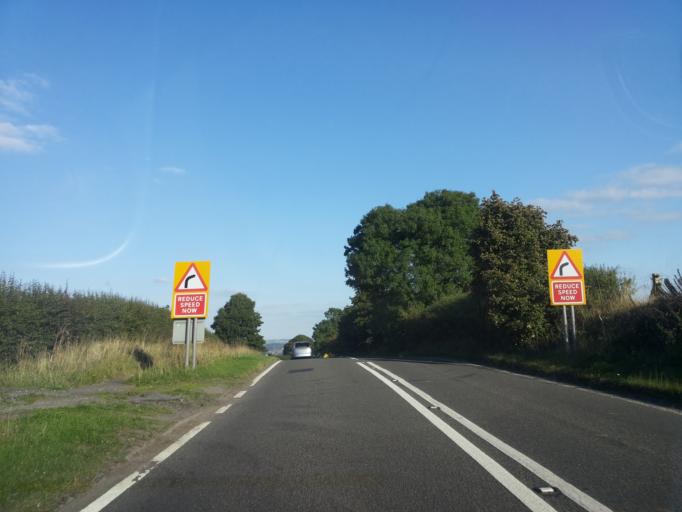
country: GB
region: England
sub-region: Derbyshire
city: Dronfield
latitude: 53.2317
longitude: -1.5230
